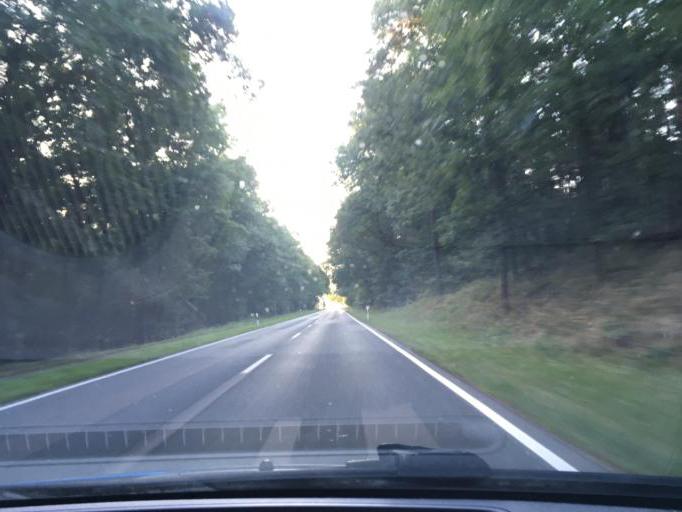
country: DE
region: Lower Saxony
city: Rehlingen
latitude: 53.0883
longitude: 10.2702
